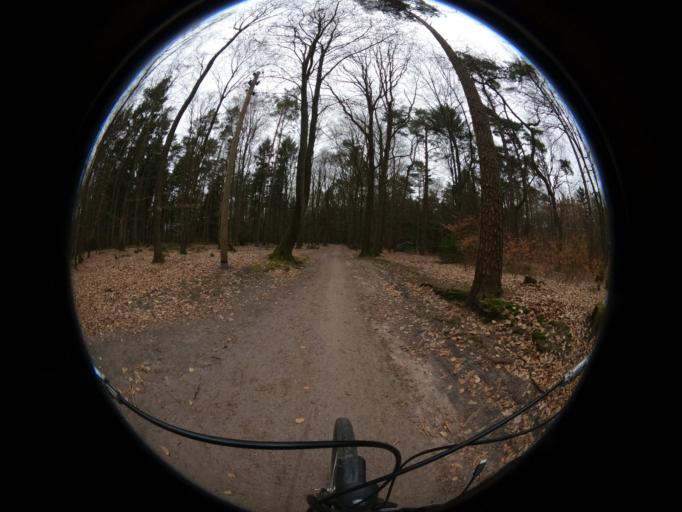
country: DE
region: Lower Saxony
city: Neu Wulmstorf
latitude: 53.4435
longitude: 9.8546
